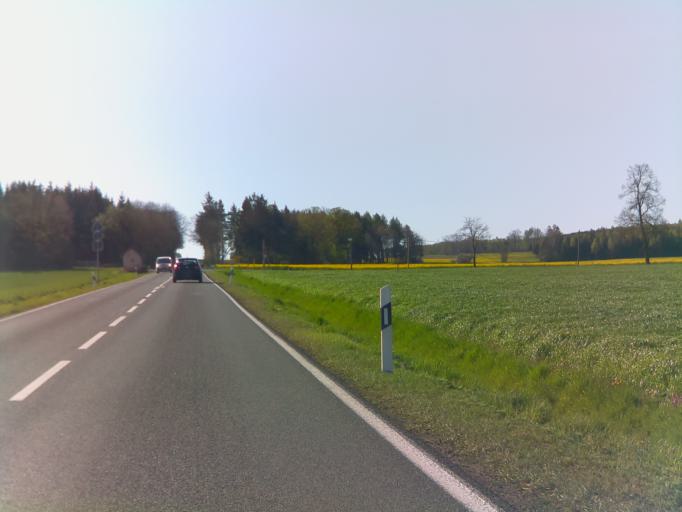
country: DE
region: Thuringia
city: Kospoda
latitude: 50.6975
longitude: 11.7669
